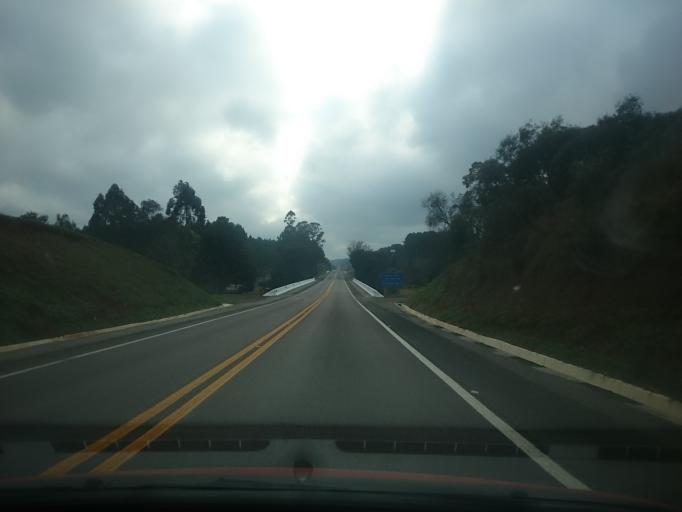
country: BR
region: Santa Catarina
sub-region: Lages
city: Lages
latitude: -27.8762
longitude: -50.4045
